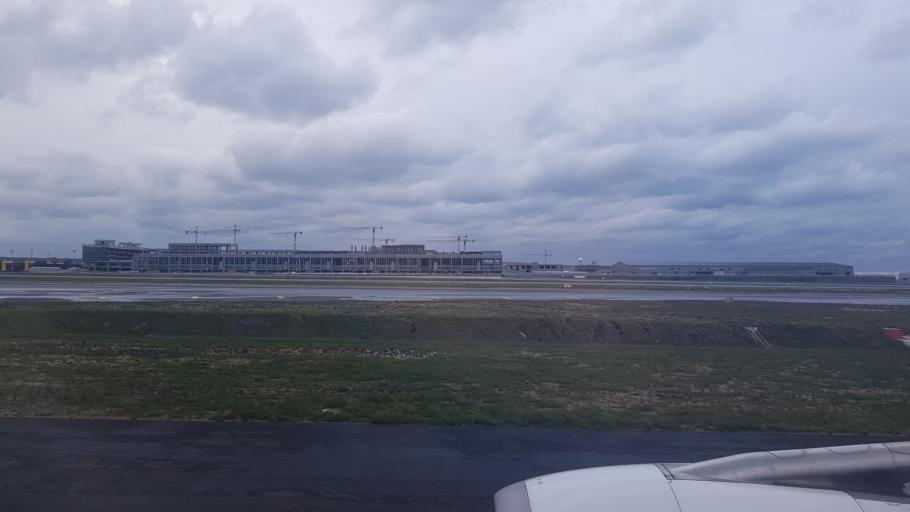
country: TR
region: Istanbul
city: Durusu
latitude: 41.2788
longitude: 28.7296
